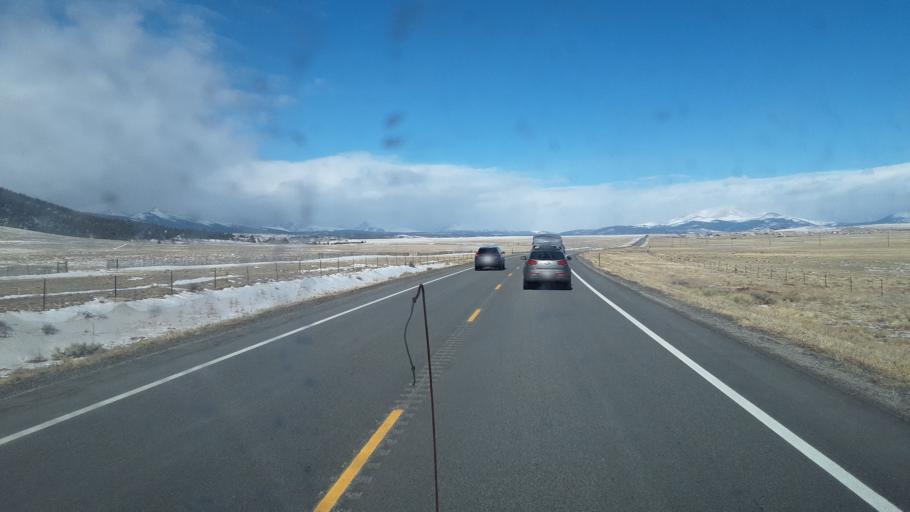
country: US
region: Colorado
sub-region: Park County
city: Fairplay
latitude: 39.0973
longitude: -105.9883
